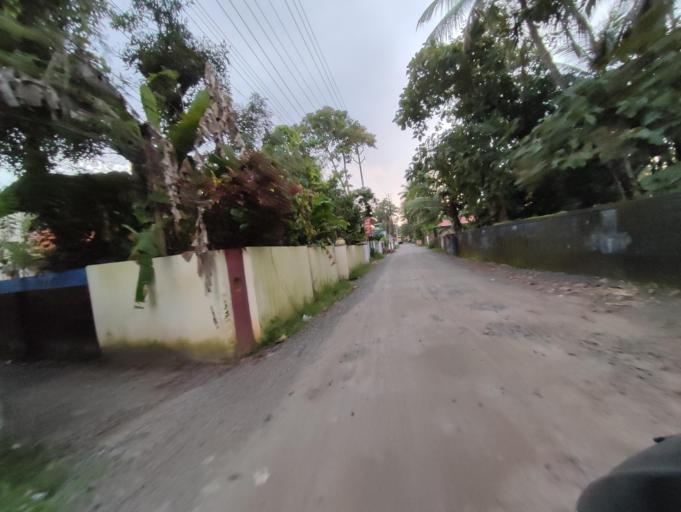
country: IN
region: Kerala
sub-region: Alappuzha
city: Vayalar
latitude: 9.6912
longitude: 76.3354
